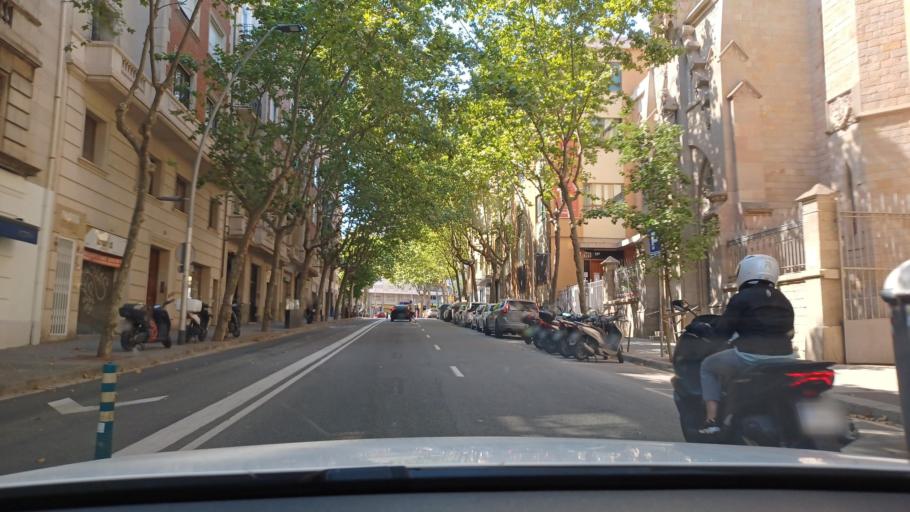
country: ES
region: Catalonia
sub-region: Provincia de Barcelona
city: les Corts
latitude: 41.3949
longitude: 2.1270
